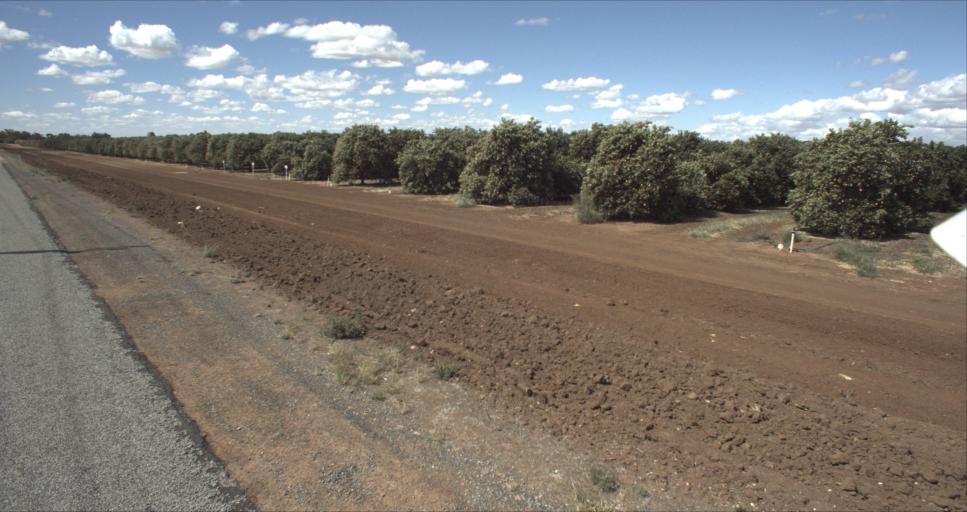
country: AU
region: New South Wales
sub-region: Leeton
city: Leeton
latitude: -34.5234
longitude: 146.2226
